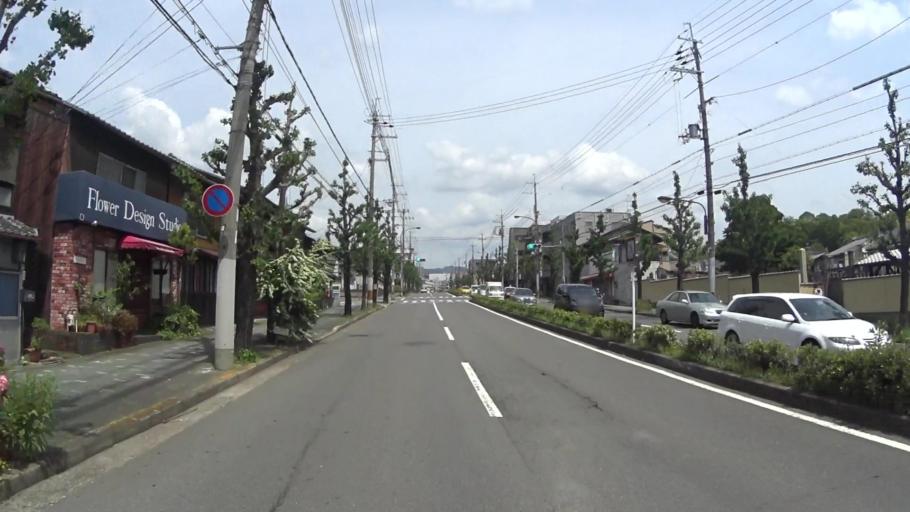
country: JP
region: Kyoto
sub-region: Kyoto-shi
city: Kamigyo-ku
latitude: 35.0371
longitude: 135.7399
